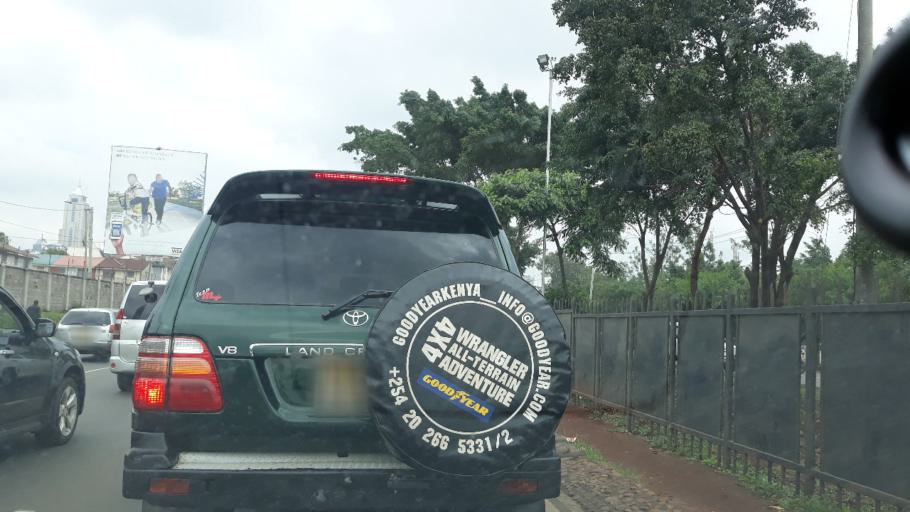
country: KE
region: Nairobi Area
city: Nairobi
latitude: -1.3076
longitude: 36.8277
